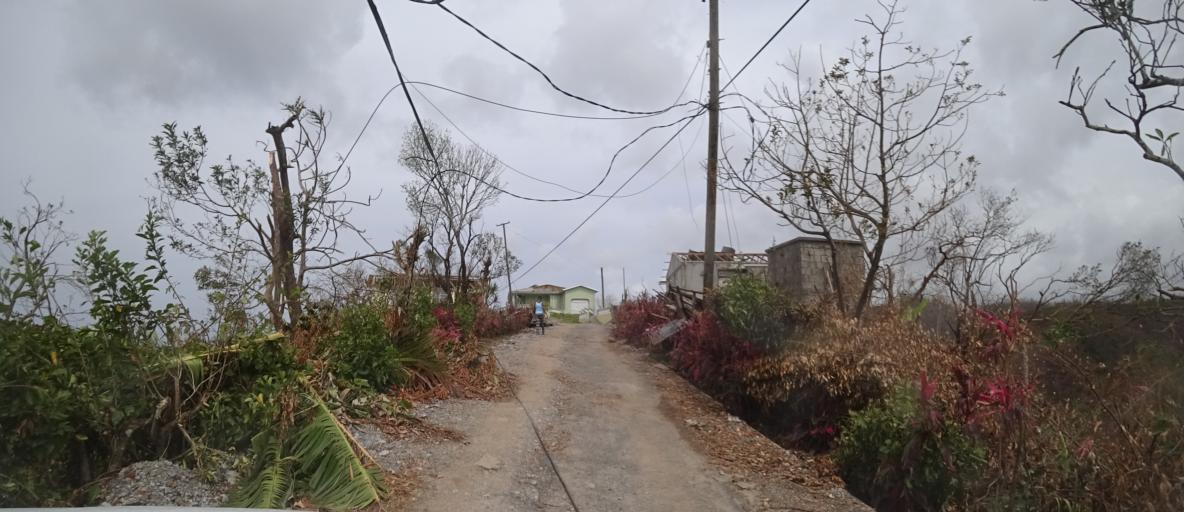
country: DM
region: Saint Andrew
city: Calibishie
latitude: 15.5897
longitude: -61.4012
